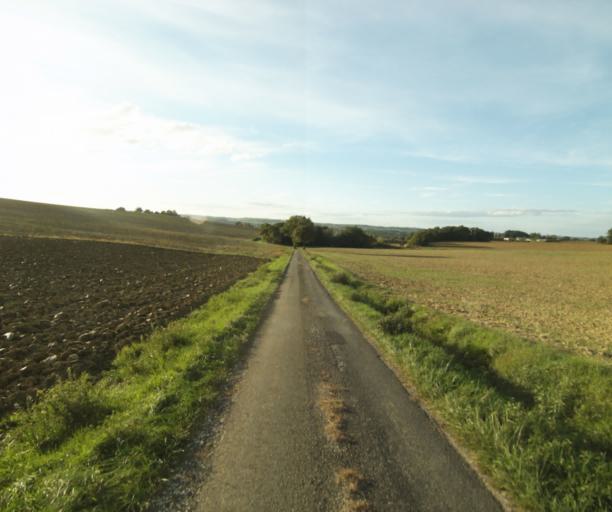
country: FR
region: Midi-Pyrenees
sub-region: Departement du Gers
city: Gondrin
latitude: 43.8759
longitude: 0.3066
